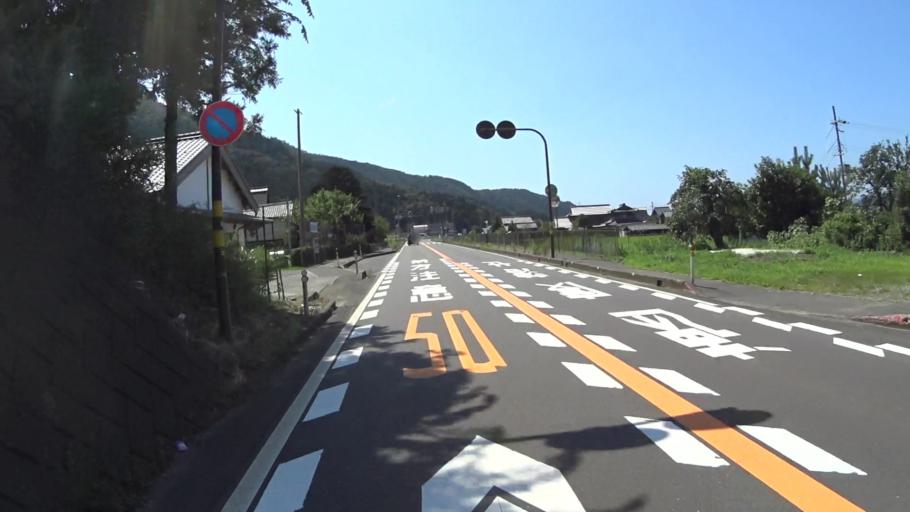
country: JP
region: Fukui
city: Obama
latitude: 35.4695
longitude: 135.8238
